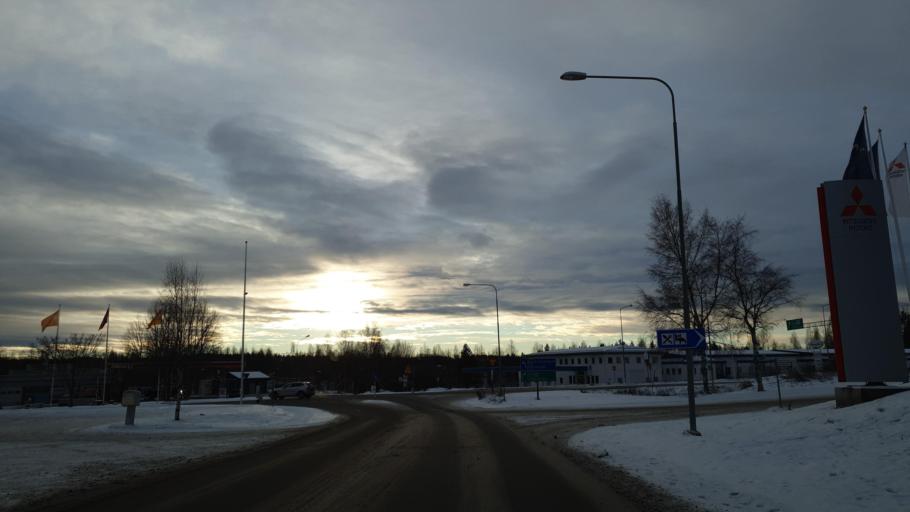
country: SE
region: Gaevleborg
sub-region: Soderhamns Kommun
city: Soderhamn
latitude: 61.3021
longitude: 17.0364
